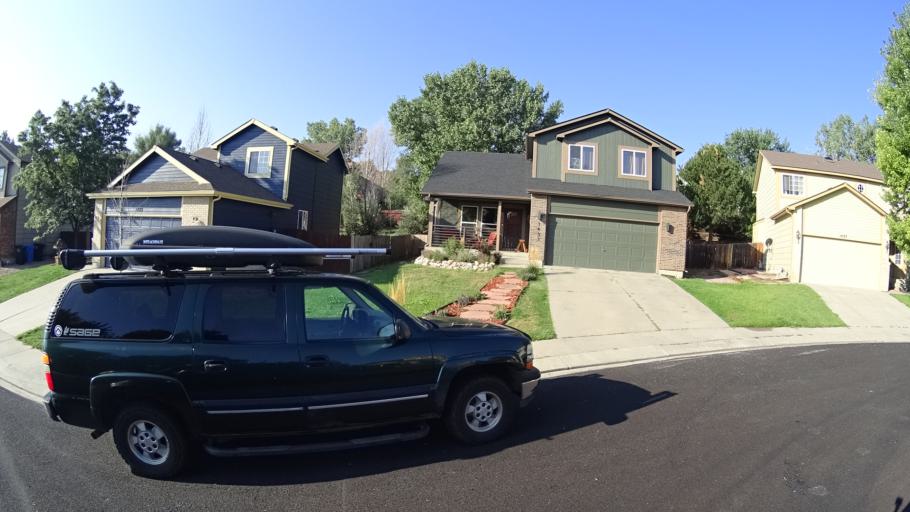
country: US
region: Colorado
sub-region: El Paso County
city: Colorado Springs
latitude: 38.8908
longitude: -104.8548
